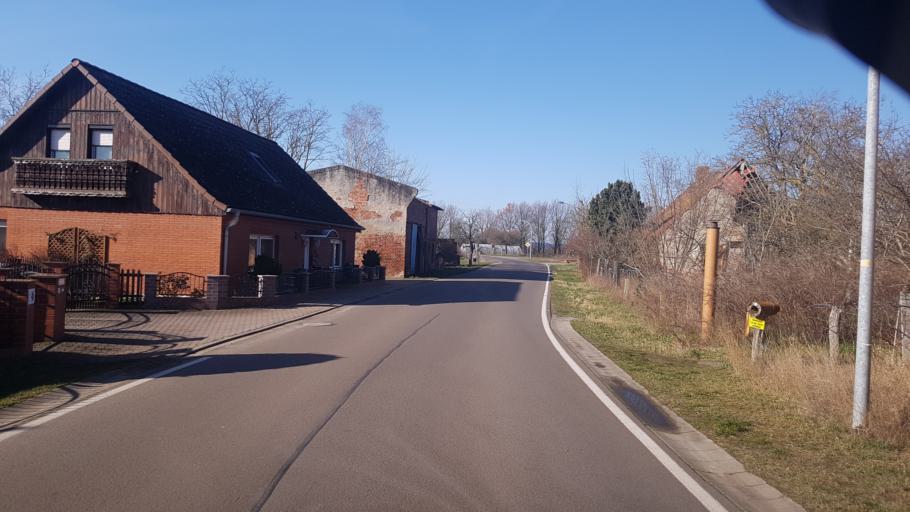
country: DE
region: Brandenburg
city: Crinitz
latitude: 51.7881
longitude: 13.7415
